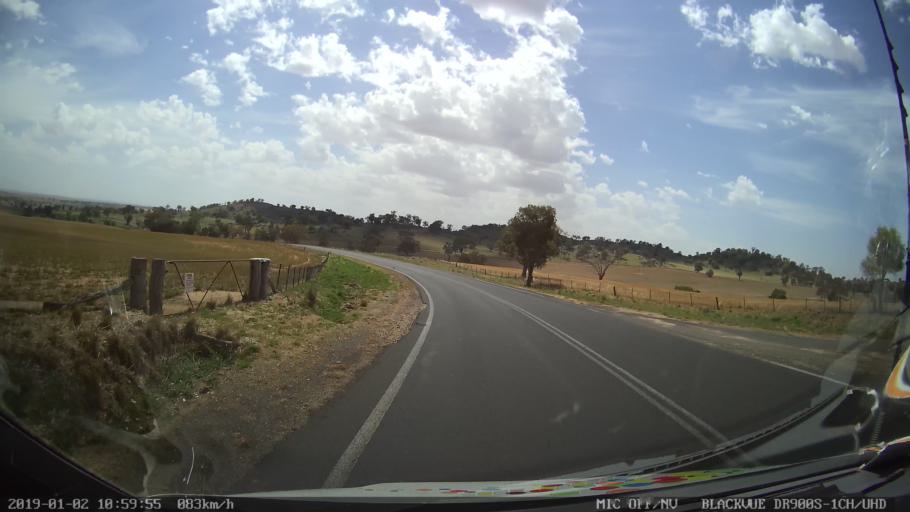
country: AU
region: New South Wales
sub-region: Cootamundra
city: Cootamundra
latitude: -34.6108
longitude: 148.3111
